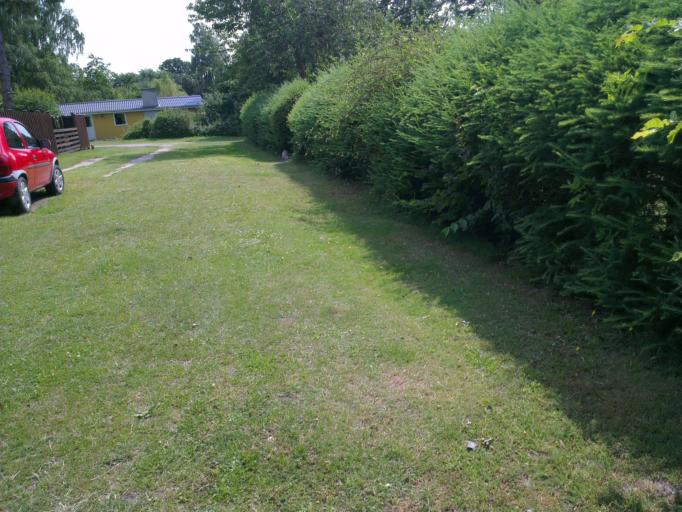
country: DK
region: Capital Region
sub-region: Halsnaes Kommune
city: Hundested
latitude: 55.9318
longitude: 11.9247
